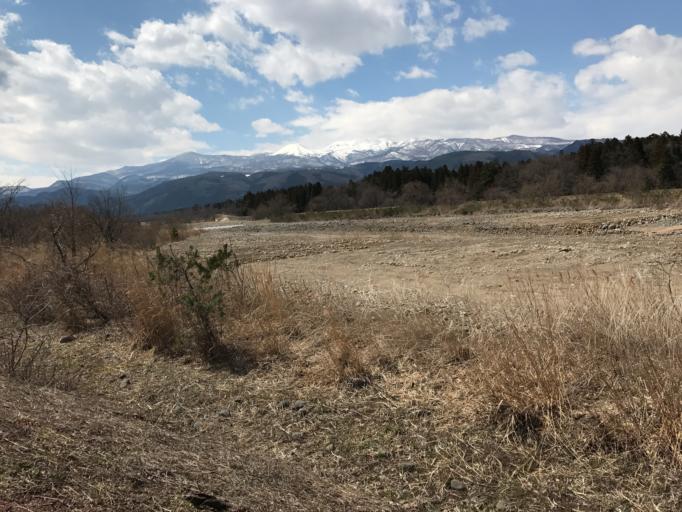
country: JP
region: Fukushima
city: Fukushima-shi
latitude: 37.7370
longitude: 140.3919
